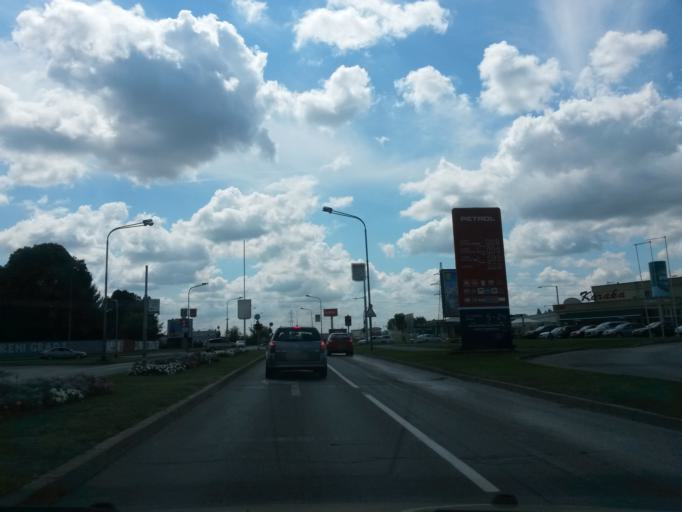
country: HR
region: Osjecko-Baranjska
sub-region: Grad Osijek
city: Osijek
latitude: 45.5495
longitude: 18.6934
